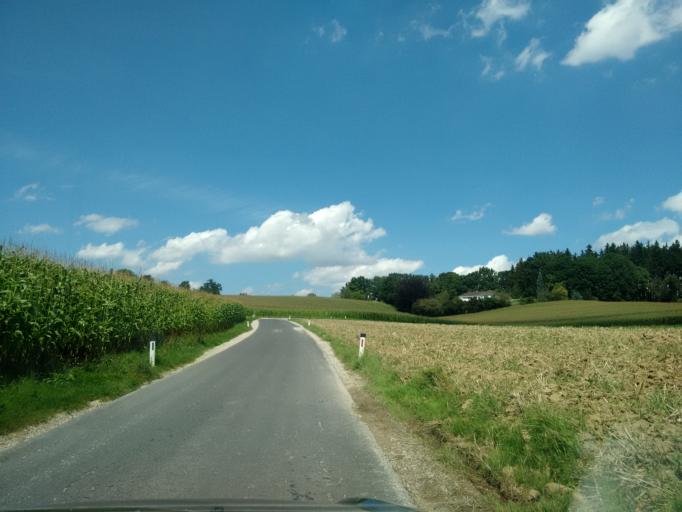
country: AT
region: Upper Austria
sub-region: Wels-Land
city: Gunskirchen
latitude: 48.1800
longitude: 13.9697
